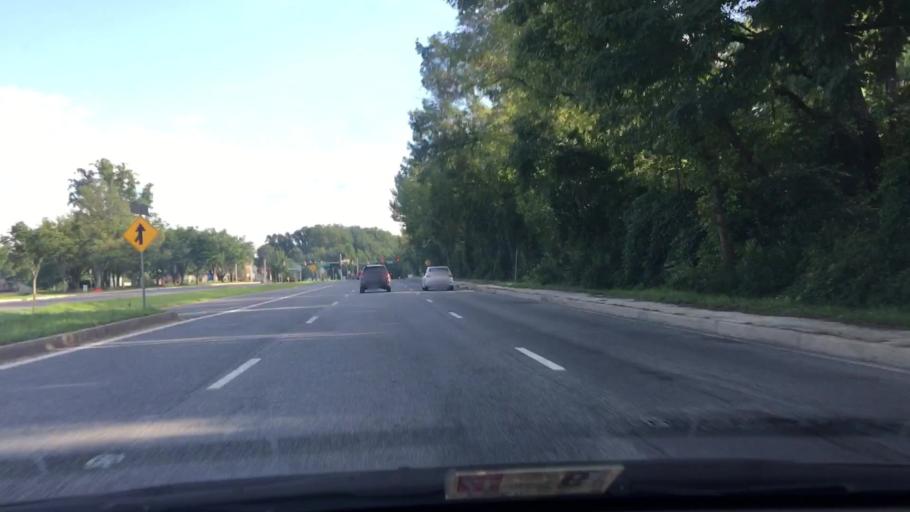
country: US
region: Maryland
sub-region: Montgomery County
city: Rossmoor
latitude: 39.1039
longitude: -77.0769
